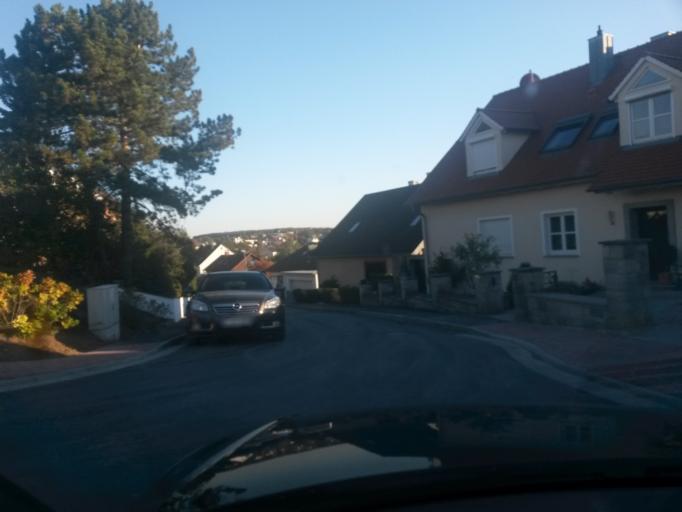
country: DE
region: Bavaria
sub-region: Regierungsbezirk Unterfranken
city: Rimpar
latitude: 49.8569
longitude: 9.9608
